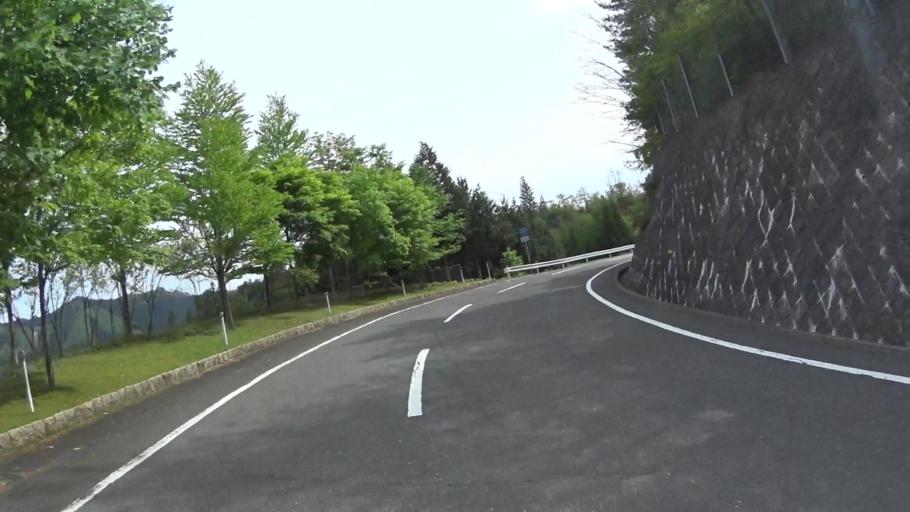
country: JP
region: Kyoto
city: Kameoka
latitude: 35.1486
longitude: 135.6246
